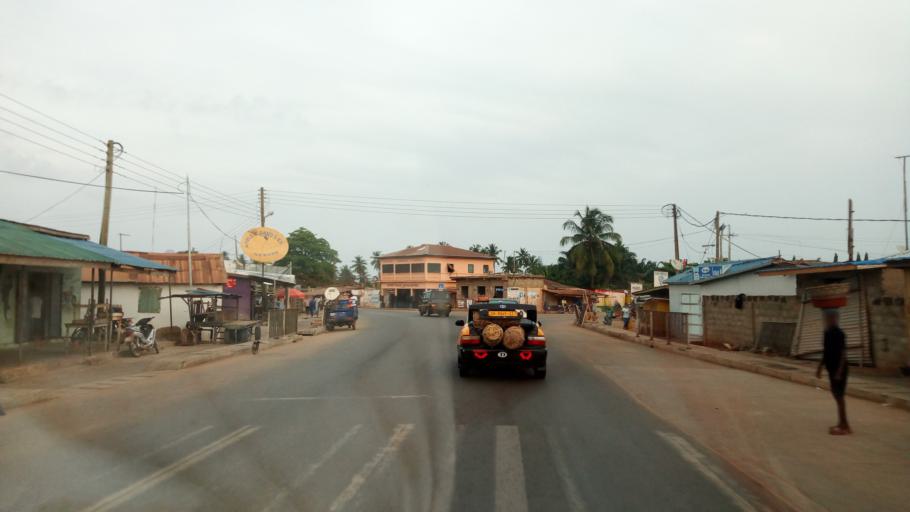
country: TG
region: Maritime
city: Lome
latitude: 6.1215
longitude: 1.1855
